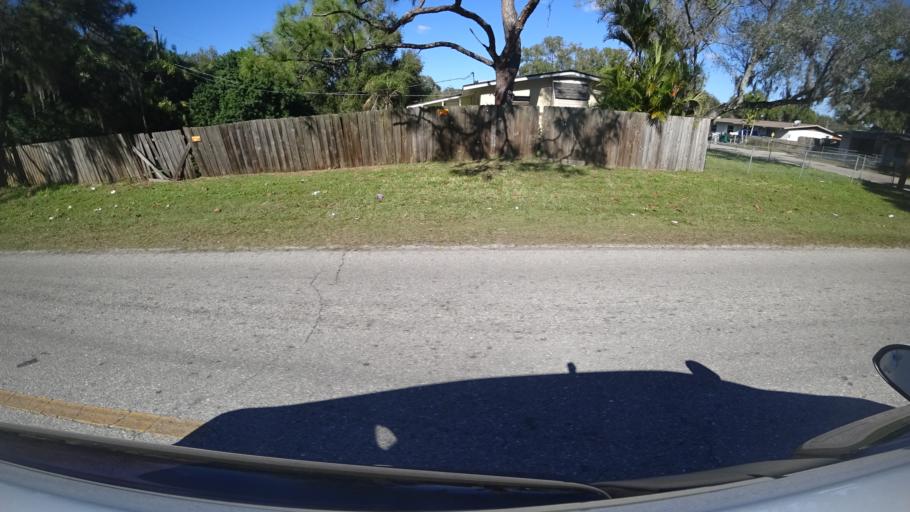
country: US
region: Florida
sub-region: Manatee County
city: Whitfield
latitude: 27.4329
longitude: -82.5526
